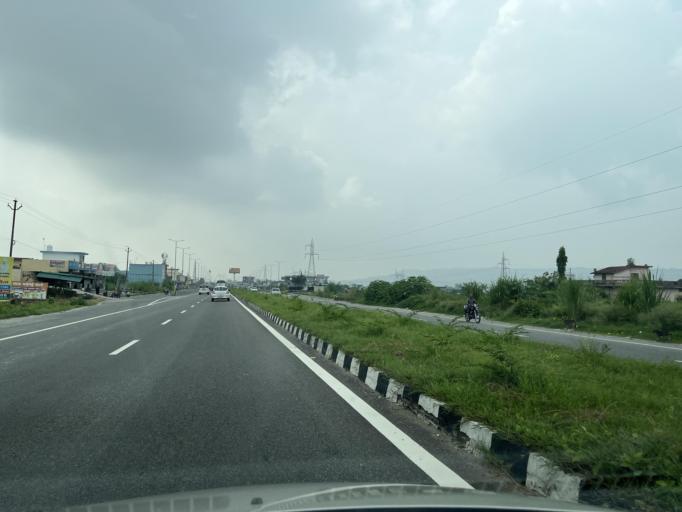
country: IN
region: Uttarakhand
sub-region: Dehradun
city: Raiwala
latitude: 30.0841
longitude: 78.1893
